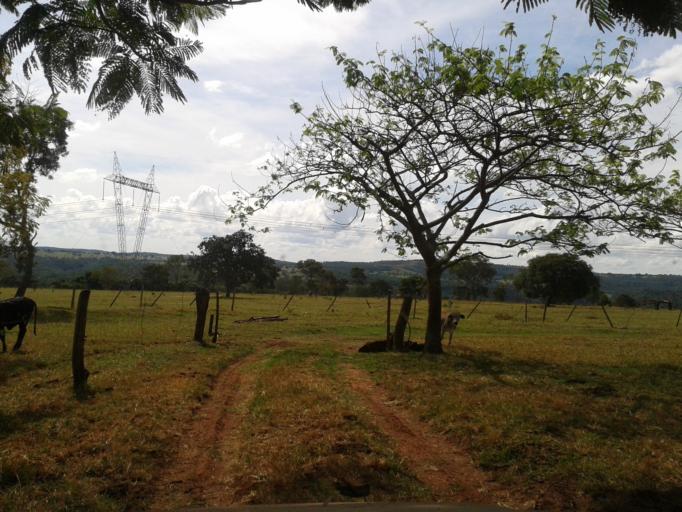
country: BR
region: Minas Gerais
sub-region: Campina Verde
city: Campina Verde
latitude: -19.4362
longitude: -49.6304
